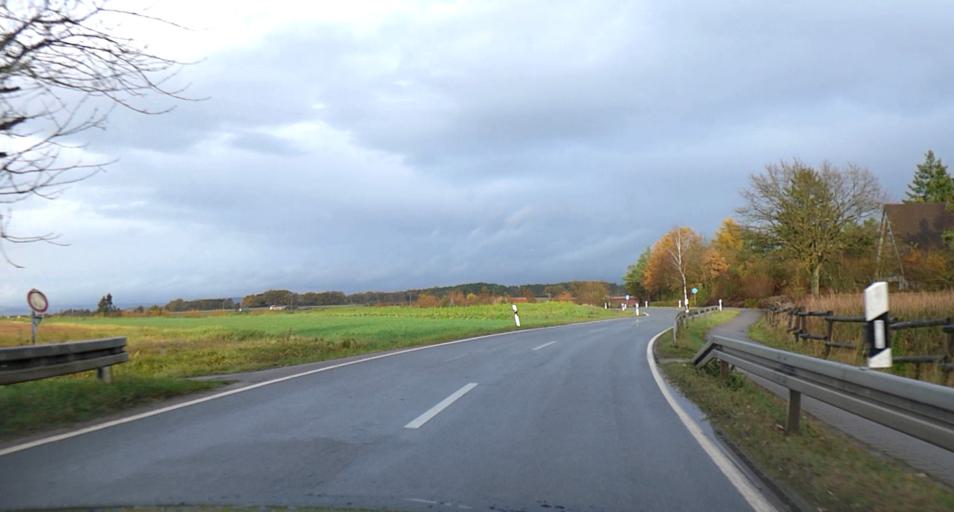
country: DE
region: Bavaria
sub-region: Upper Franconia
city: Langensendelbach
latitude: 49.6400
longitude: 11.0557
